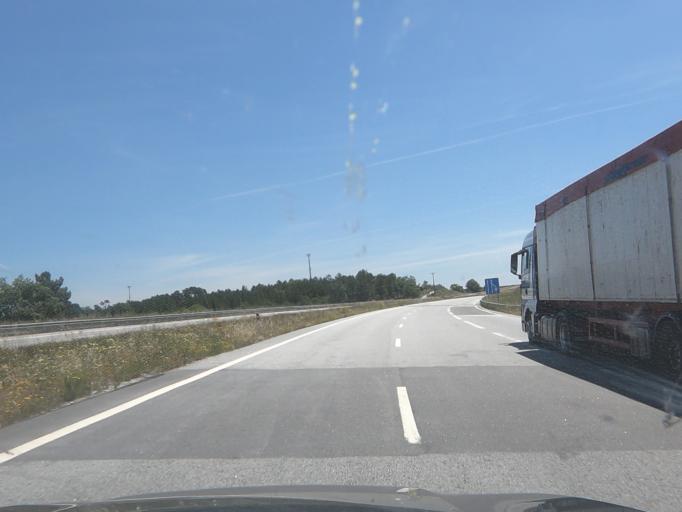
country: PT
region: Guarda
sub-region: Pinhel
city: Pinhel
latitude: 40.6105
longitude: -7.0054
